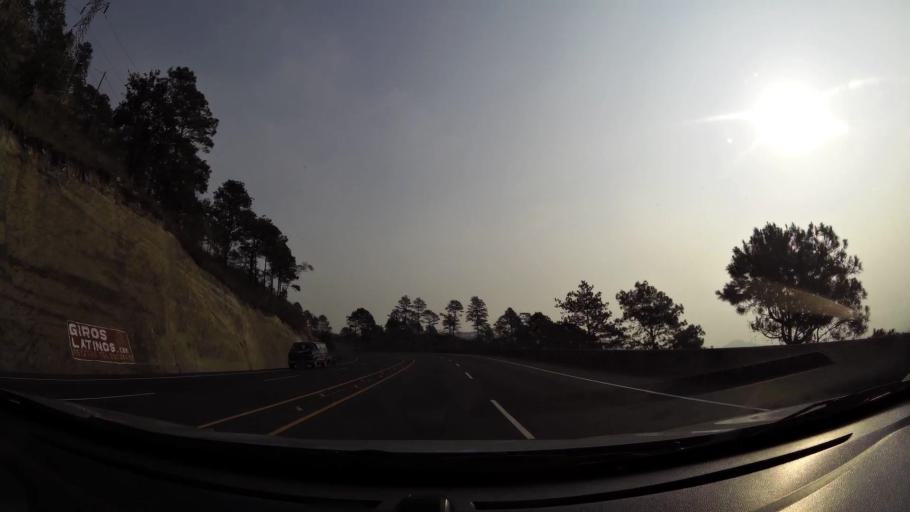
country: HN
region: Francisco Morazan
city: Zambrano
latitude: 14.2475
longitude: -87.3759
